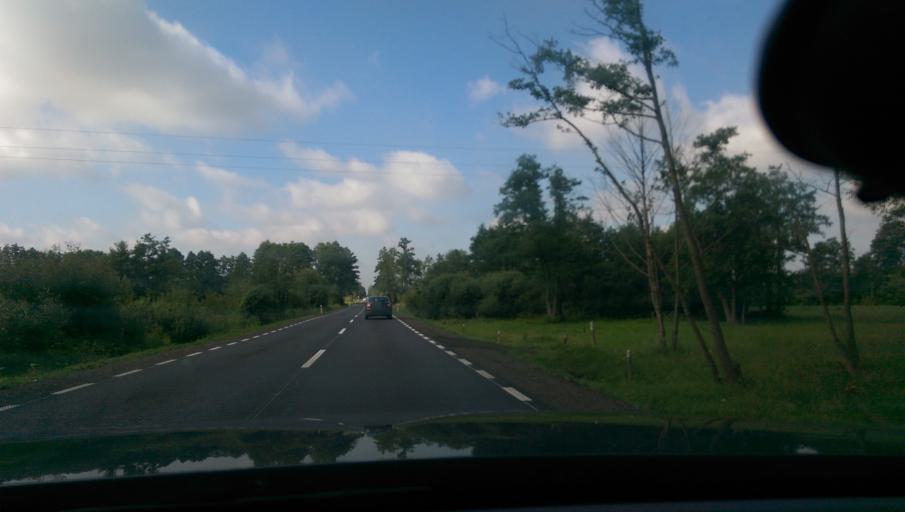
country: PL
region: Masovian Voivodeship
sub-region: Powiat plonski
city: Sochocin
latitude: 52.7237
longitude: 20.5076
